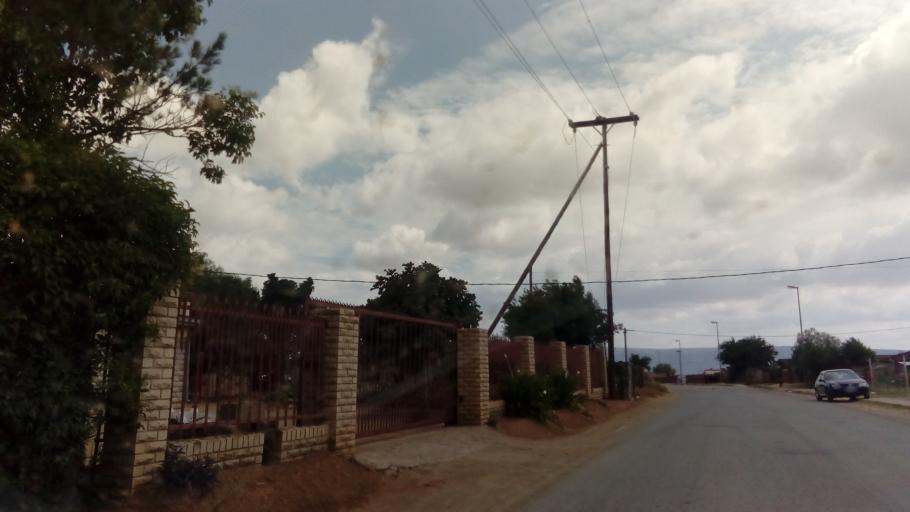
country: LS
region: Maseru
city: Maseru
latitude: -29.3830
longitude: 27.5294
